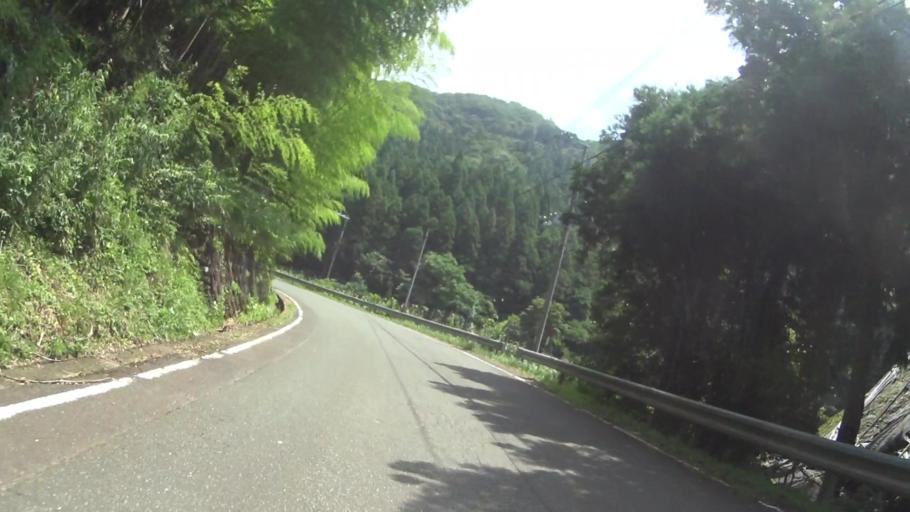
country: JP
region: Kyoto
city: Maizuru
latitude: 35.3098
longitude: 135.4337
